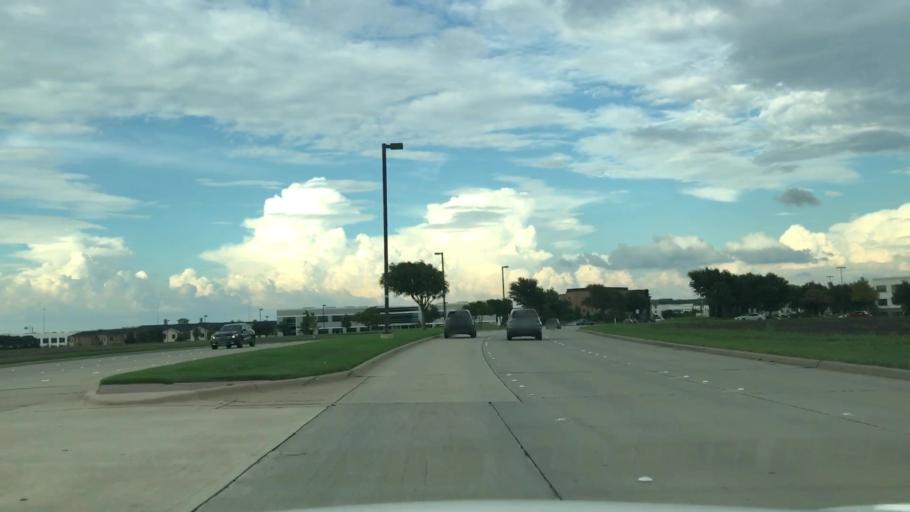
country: US
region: Texas
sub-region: Collin County
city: Frisco
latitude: 33.0863
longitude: -96.8100
